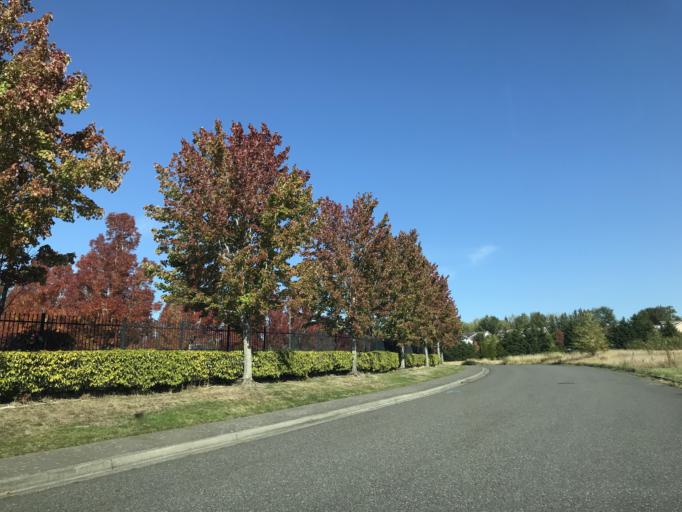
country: US
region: Washington
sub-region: Whatcom County
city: Bellingham
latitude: 48.8088
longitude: -122.4953
